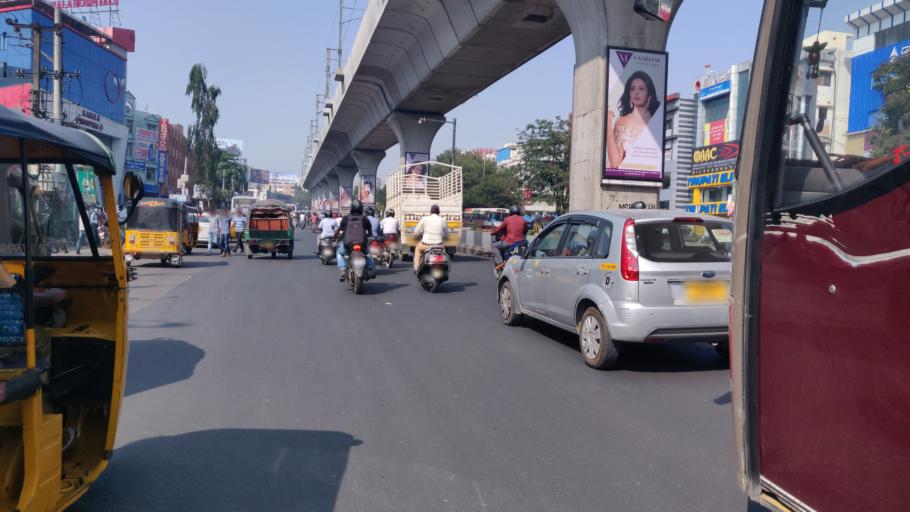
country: IN
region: Telangana
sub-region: Rangareddi
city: Gaddi Annaram
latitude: 17.3685
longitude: 78.5229
